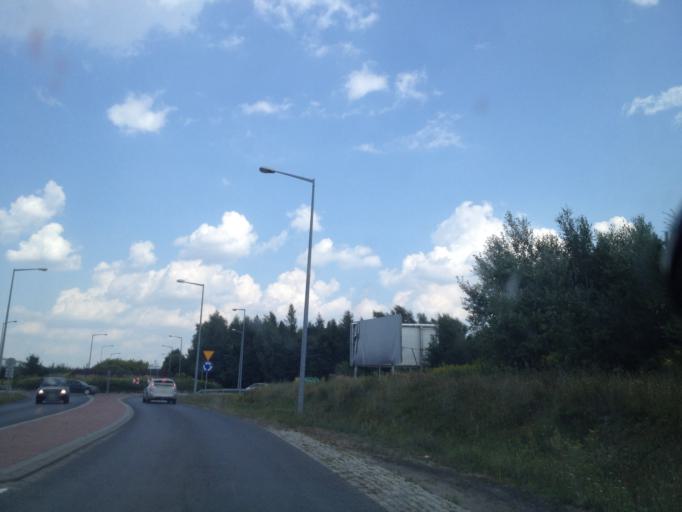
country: PL
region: Greater Poland Voivodeship
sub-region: Powiat poznanski
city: Kornik
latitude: 52.2478
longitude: 17.0527
